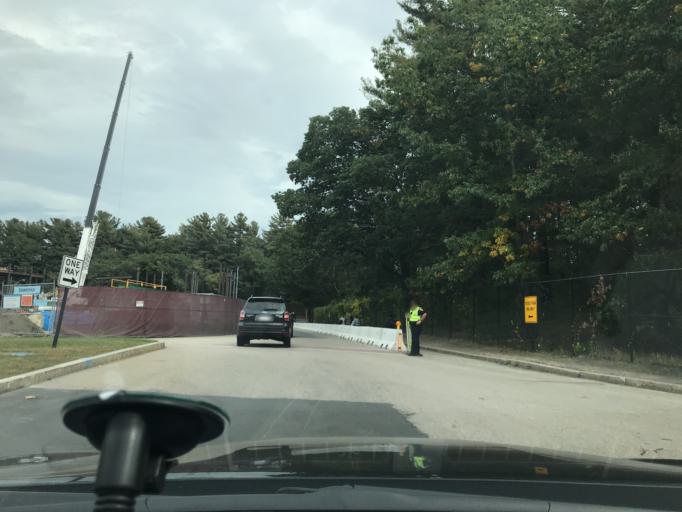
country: US
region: Massachusetts
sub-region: Middlesex County
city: Watertown
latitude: 42.3361
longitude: -71.1657
